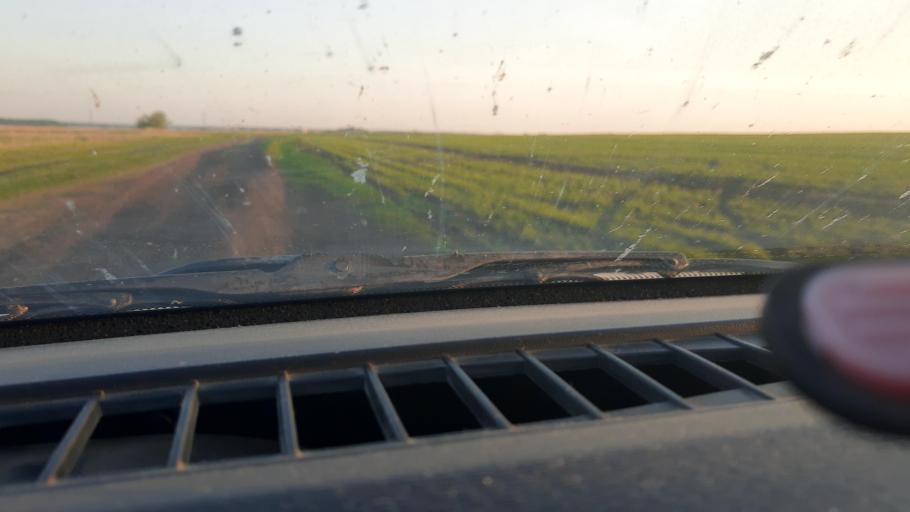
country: RU
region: Bashkortostan
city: Asanovo
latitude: 54.8554
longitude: 55.5850
